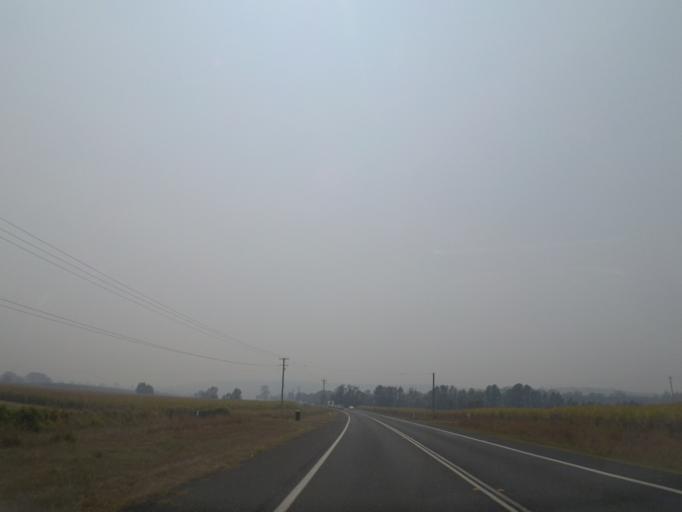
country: AU
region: New South Wales
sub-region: Clarence Valley
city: Maclean
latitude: -29.5672
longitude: 153.1328
